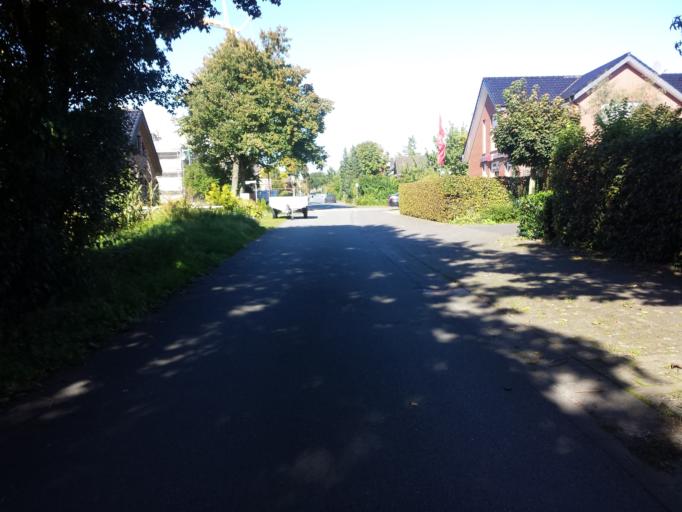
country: DE
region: North Rhine-Westphalia
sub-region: Regierungsbezirk Detmold
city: Langenberg
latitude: 51.7639
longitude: 8.3140
